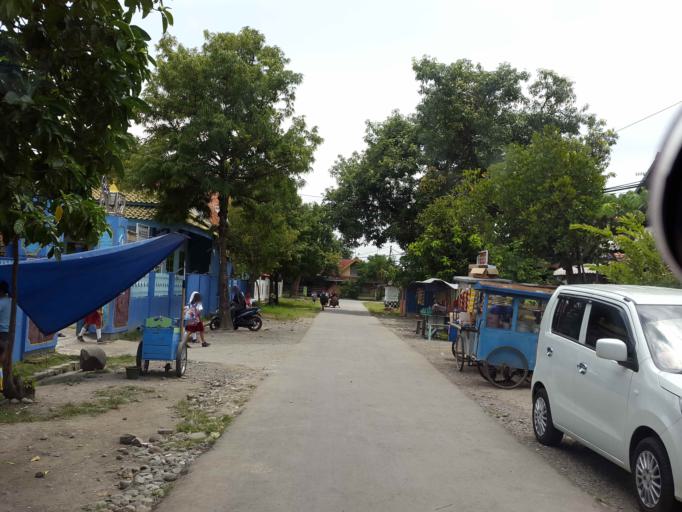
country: ID
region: Central Java
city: Pemalang
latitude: -6.8928
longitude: 109.3882
